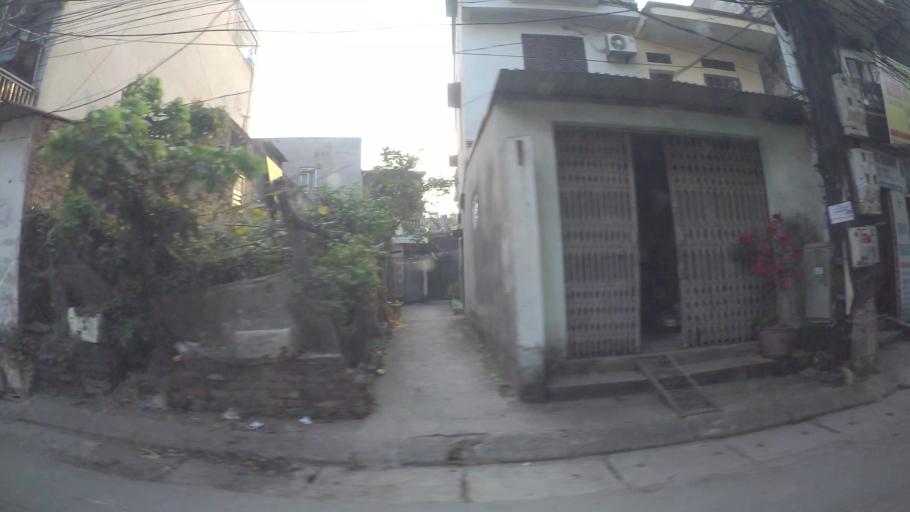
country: VN
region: Ha Noi
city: Van Dien
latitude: 20.9317
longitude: 105.8356
